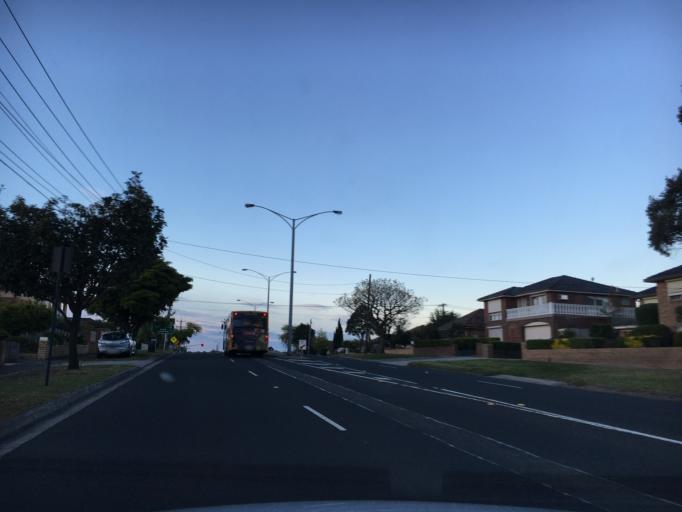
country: AU
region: Victoria
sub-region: Monash
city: Chadstone
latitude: -37.8987
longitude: 145.1057
